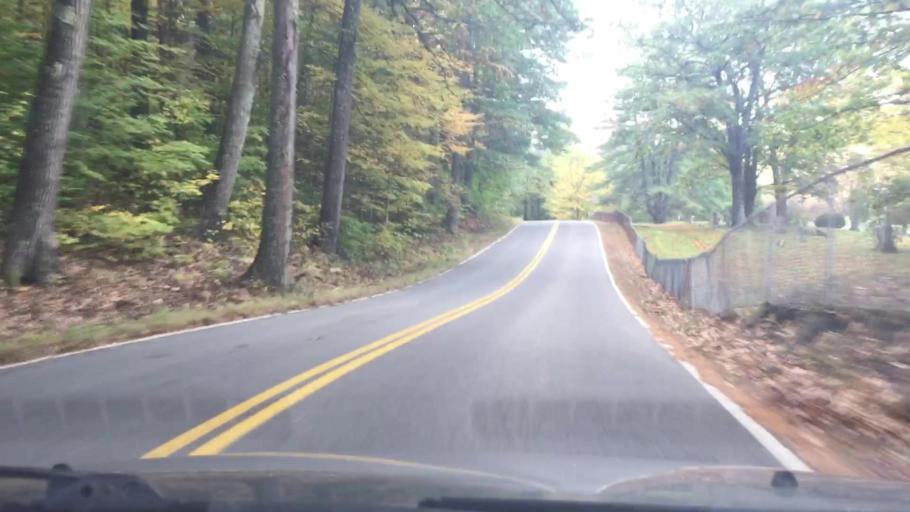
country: US
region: New Hampshire
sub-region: Cheshire County
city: Keene
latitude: 42.9426
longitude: -72.2664
